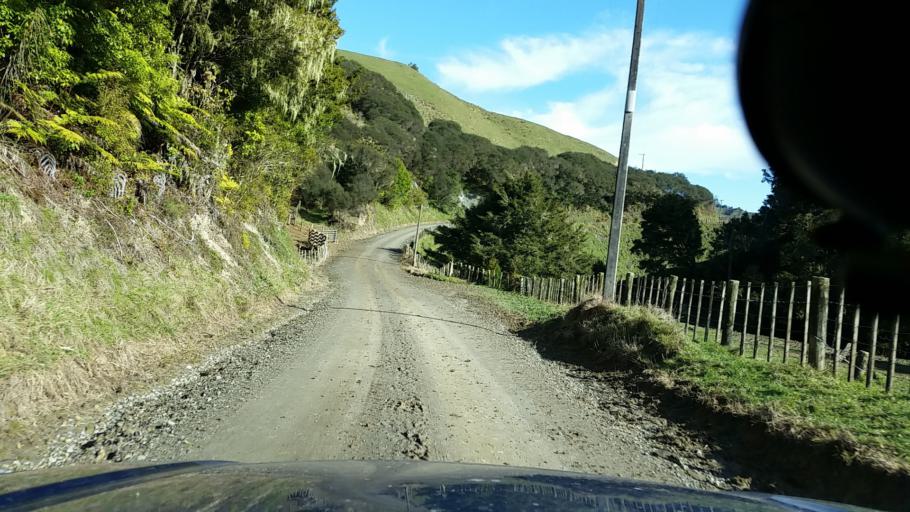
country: NZ
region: Taranaki
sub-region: New Plymouth District
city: Waitara
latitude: -39.0506
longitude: 174.7620
